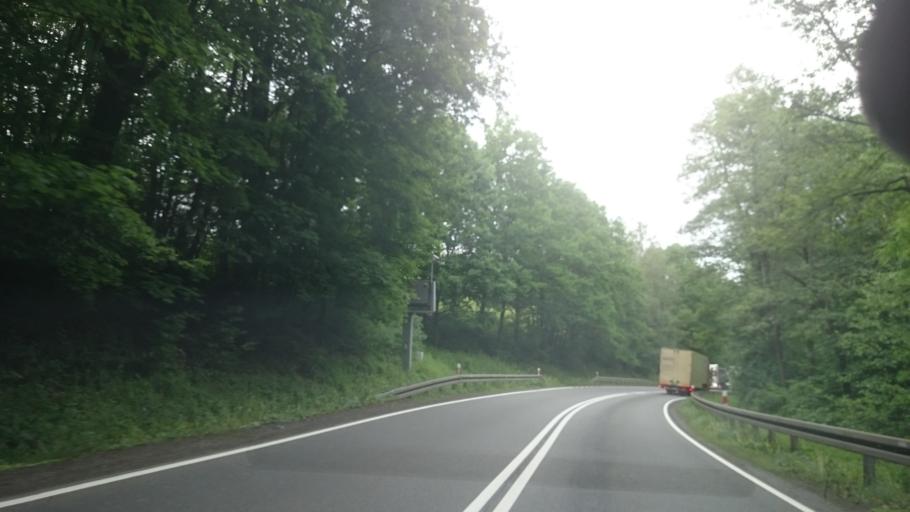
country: PL
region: Lower Silesian Voivodeship
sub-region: Powiat zabkowicki
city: Zloty Stok
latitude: 50.4371
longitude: 16.8224
